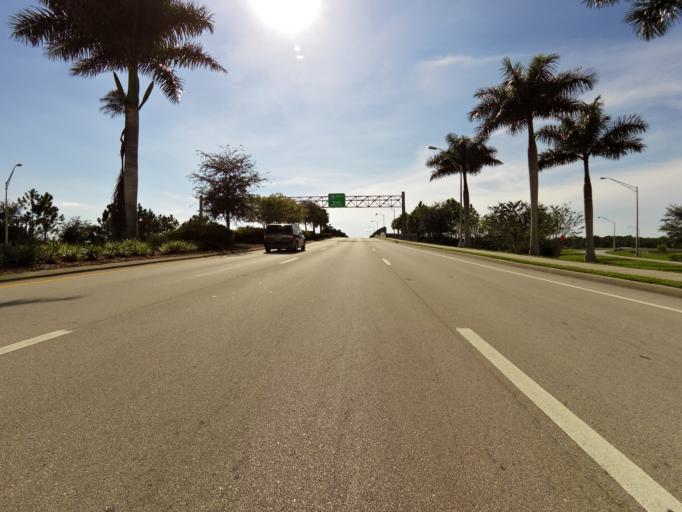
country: US
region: Florida
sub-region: Collier County
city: Golden Gate
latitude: 26.1744
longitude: -81.7321
